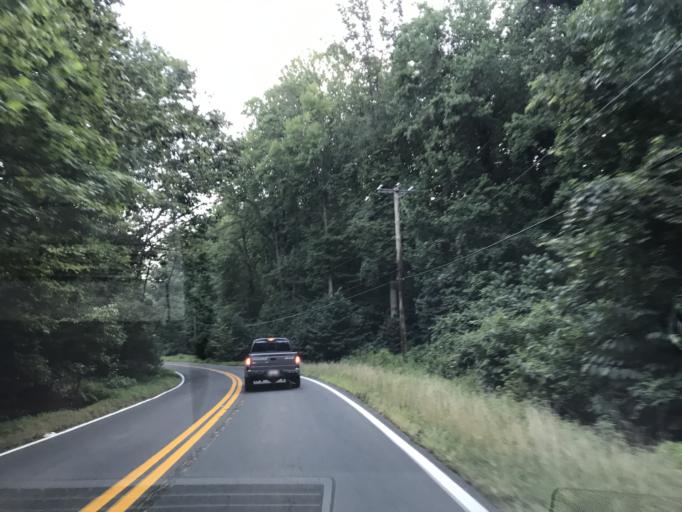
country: US
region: Maryland
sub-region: Cecil County
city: Charlestown
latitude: 39.4902
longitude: -75.9790
